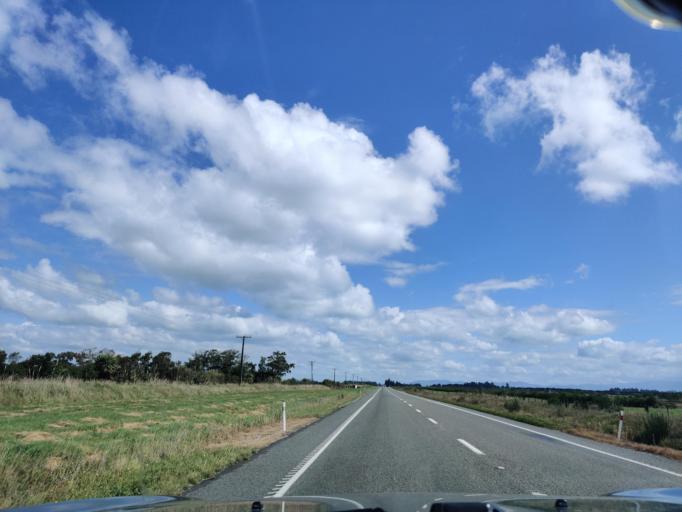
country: NZ
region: Canterbury
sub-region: Ashburton District
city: Tinwald
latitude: -44.0353
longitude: 171.4576
